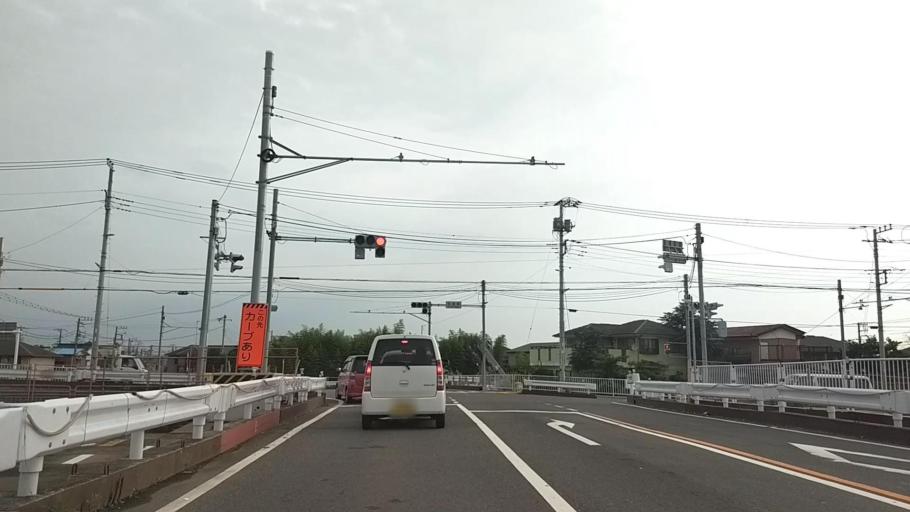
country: JP
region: Kanagawa
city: Isehara
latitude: 35.3592
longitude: 139.2982
